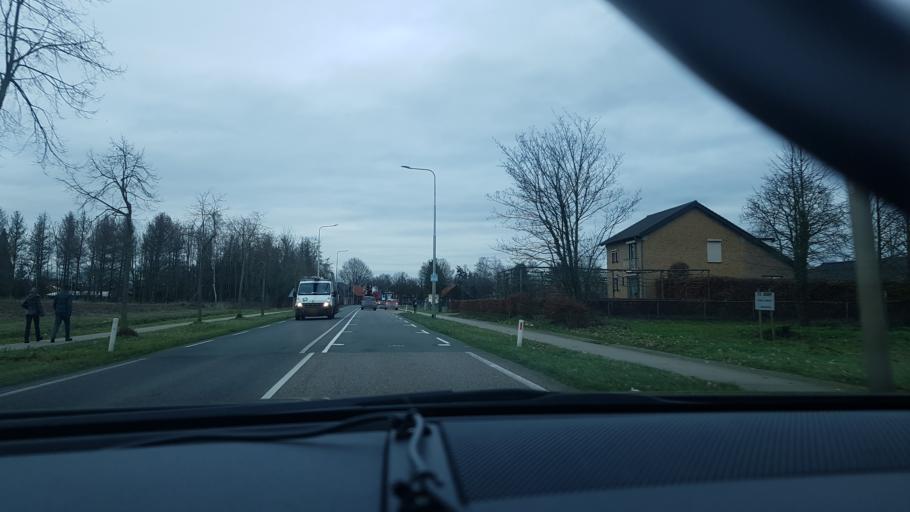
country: NL
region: Limburg
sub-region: Gemeente Leudal
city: Heythuysen
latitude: 51.2578
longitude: 5.9147
